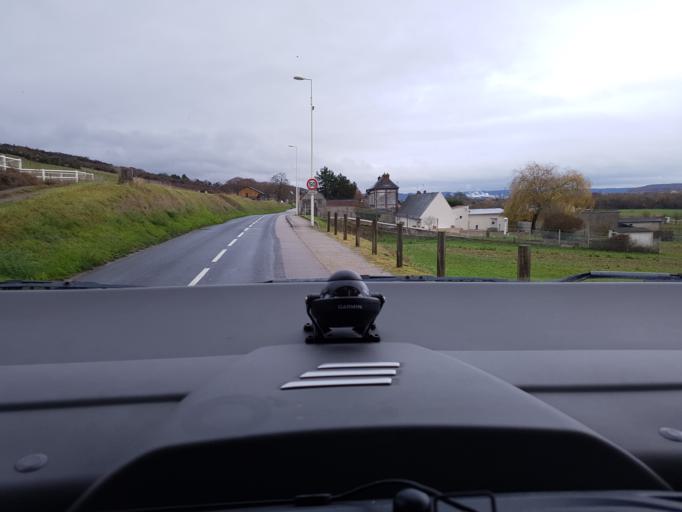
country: FR
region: Haute-Normandie
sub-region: Departement de l'Eure
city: Igoville
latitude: 49.3203
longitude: 1.1282
